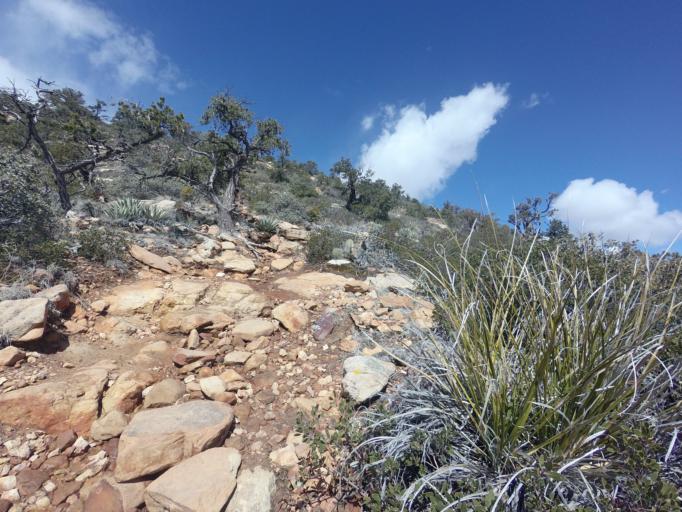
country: US
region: Arizona
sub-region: Yavapai County
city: West Sedona
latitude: 34.9136
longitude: -111.8808
